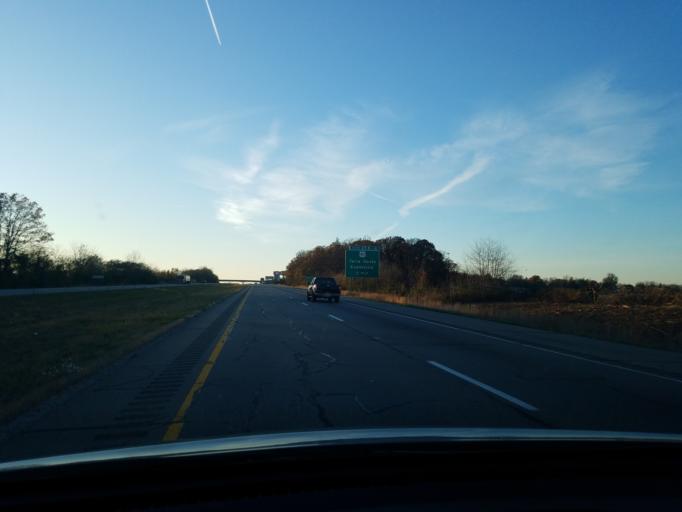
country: US
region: Indiana
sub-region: Gibson County
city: Haubstadt
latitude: 38.1662
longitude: -87.5229
